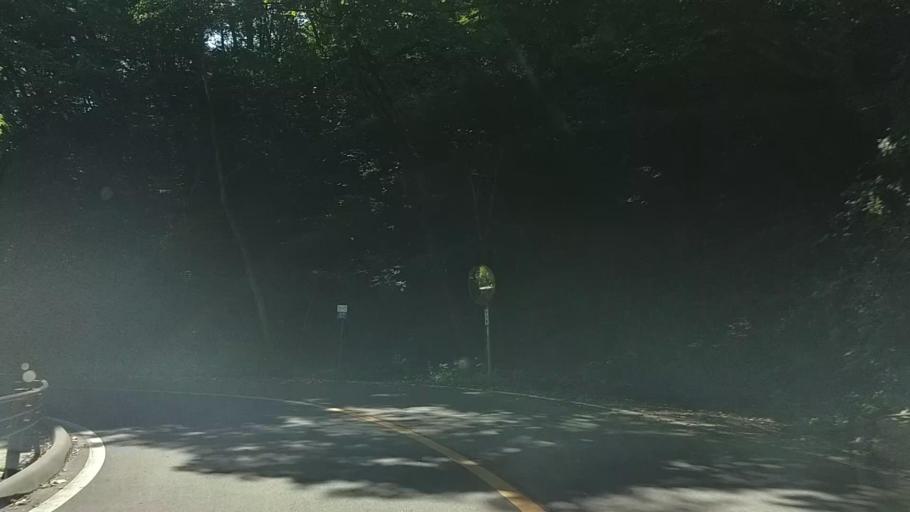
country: JP
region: Gunma
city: Annaka
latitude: 36.3567
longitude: 138.6991
